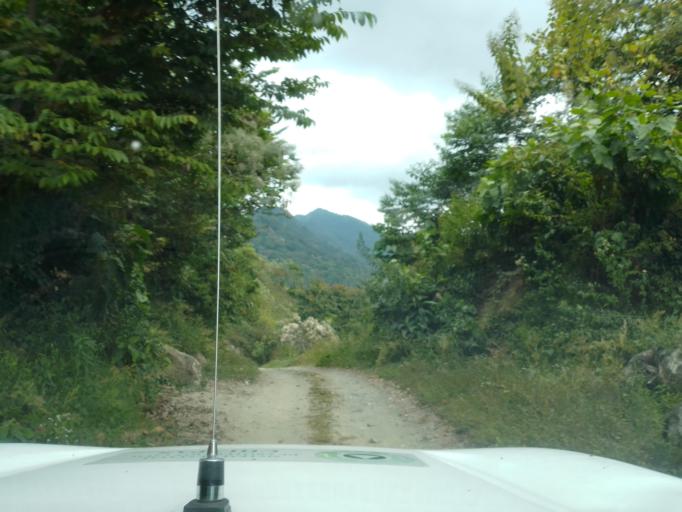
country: MX
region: Chiapas
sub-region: Union Juarez
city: Santo Domingo
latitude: 15.0557
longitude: -92.0976
